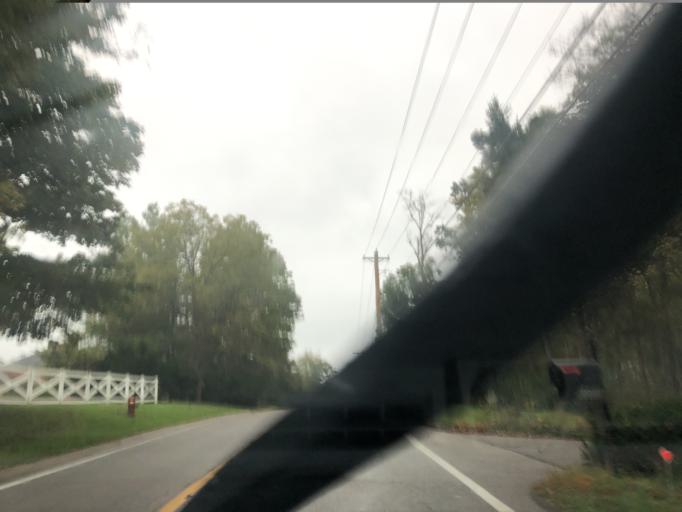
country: US
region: Ohio
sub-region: Clermont County
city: Mulberry
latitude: 39.2080
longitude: -84.2449
